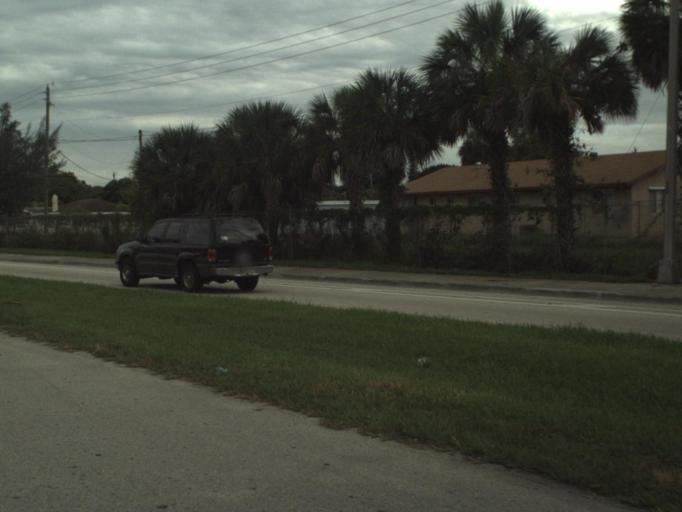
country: US
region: Florida
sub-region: Palm Beach County
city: Royal Palm Estates
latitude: 26.6784
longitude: -80.1239
